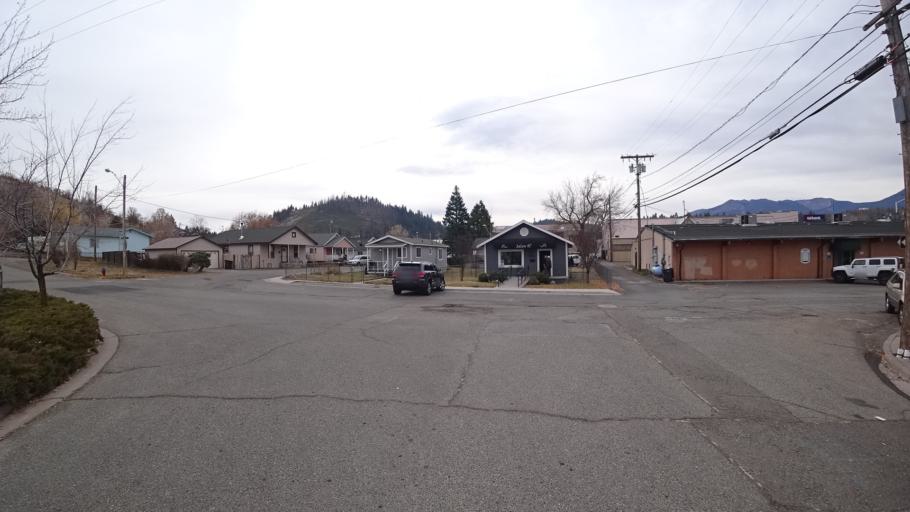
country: US
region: California
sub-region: Siskiyou County
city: Weed
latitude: 41.4252
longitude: -122.3836
